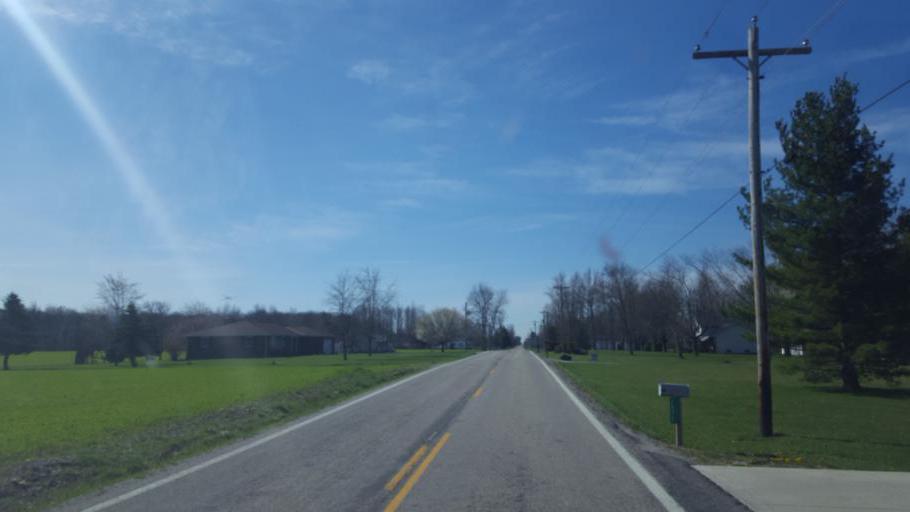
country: US
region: Ohio
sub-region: Morrow County
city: Cardington
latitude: 40.5522
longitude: -82.9624
